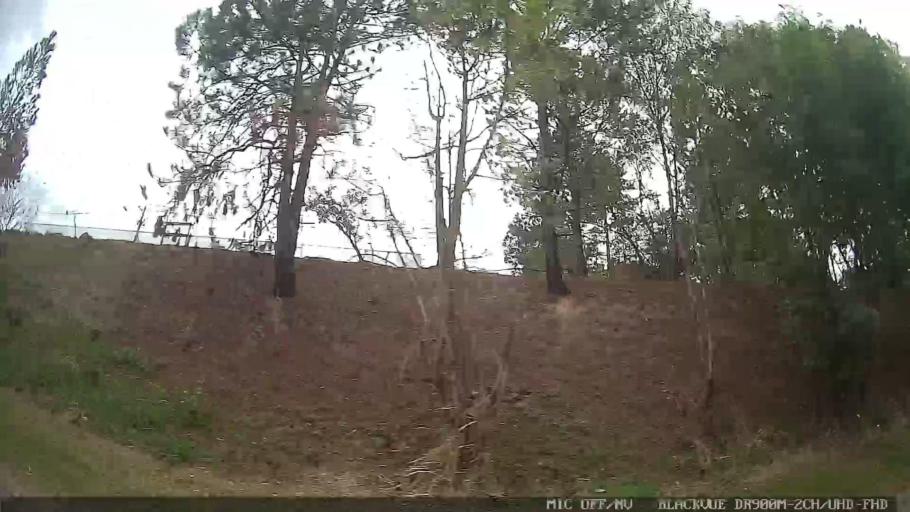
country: BR
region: Sao Paulo
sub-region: Indaiatuba
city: Indaiatuba
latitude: -23.0984
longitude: -47.1937
